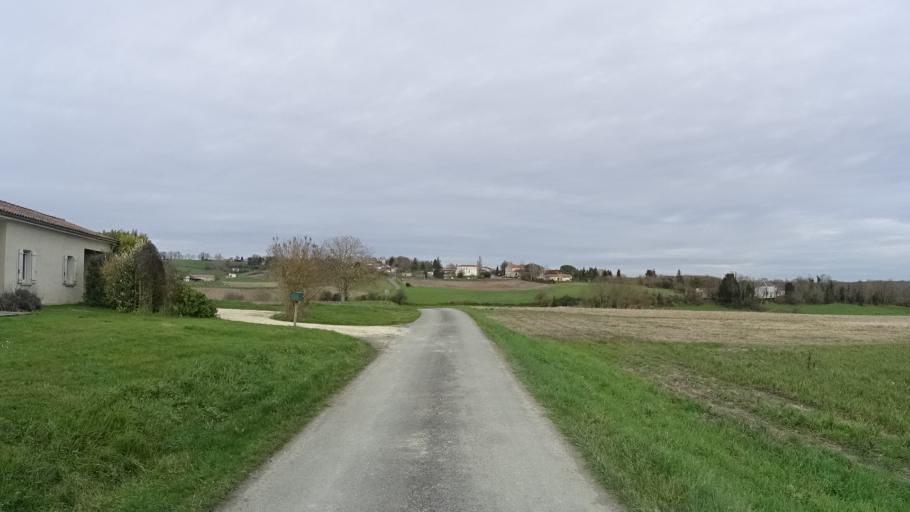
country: FR
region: Aquitaine
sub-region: Departement de la Dordogne
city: Saint-Aulaye
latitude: 45.2622
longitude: 0.1686
